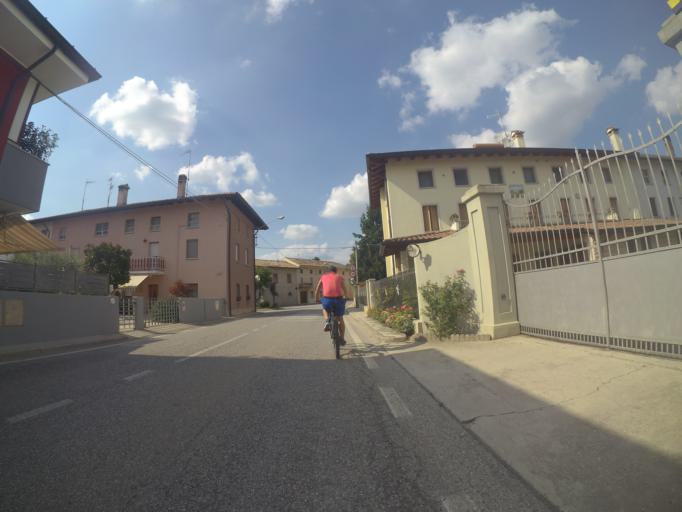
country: IT
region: Friuli Venezia Giulia
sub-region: Provincia di Udine
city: Basiliano-Vissandone
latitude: 46.0553
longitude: 13.0858
